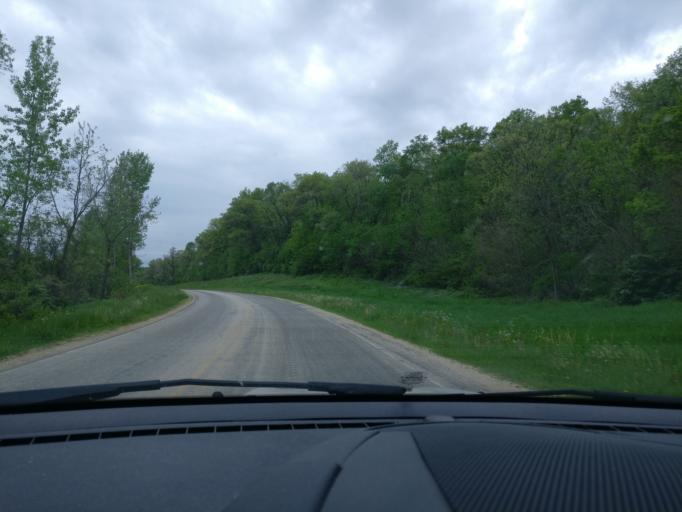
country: US
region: Wisconsin
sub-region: Lafayette County
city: Darlington
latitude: 42.7728
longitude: -90.0024
